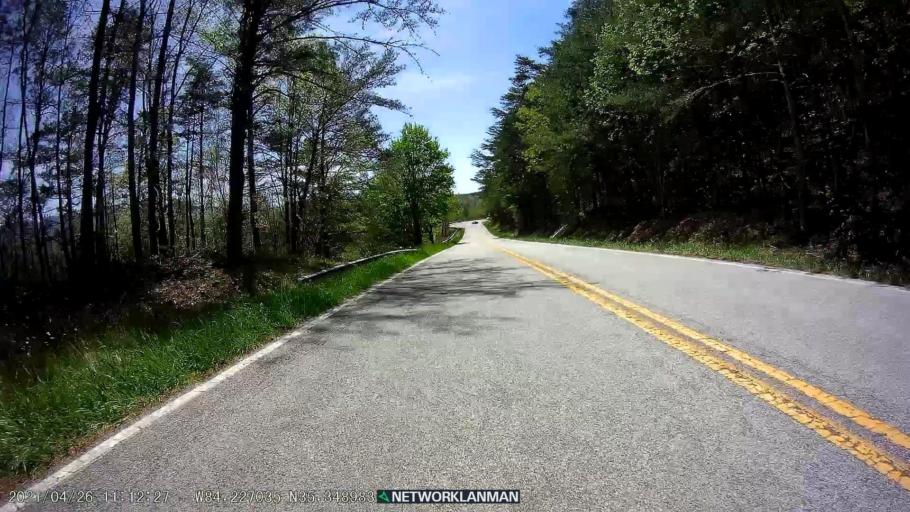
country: US
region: Tennessee
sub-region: Monroe County
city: Madisonville
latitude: 35.3488
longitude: -84.2267
